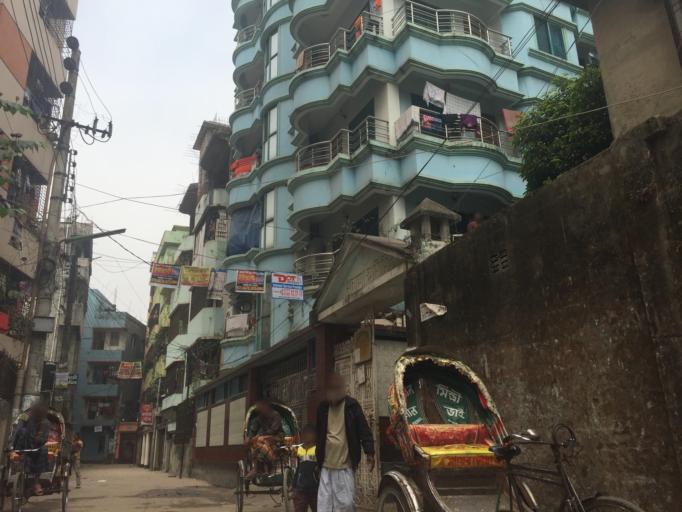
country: BD
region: Dhaka
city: Azimpur
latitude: 23.7806
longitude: 90.3657
